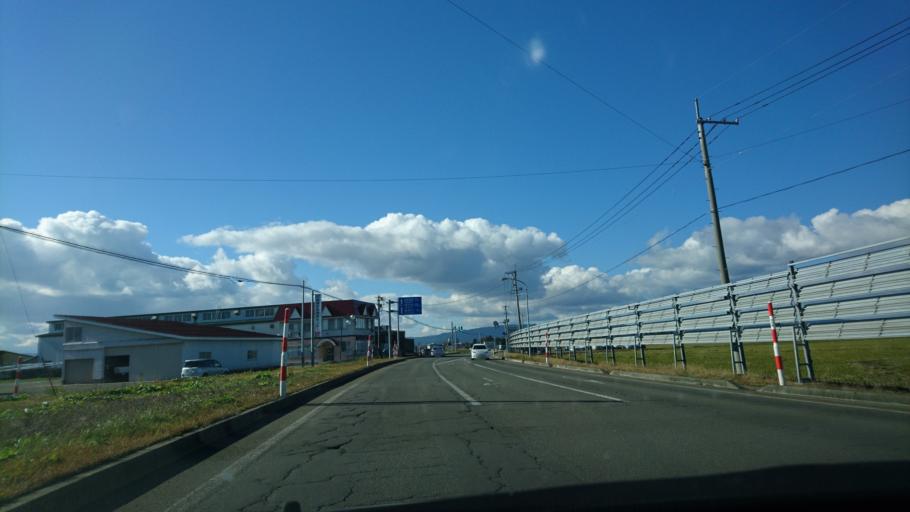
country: JP
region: Akita
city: Yokotemachi
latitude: 39.2659
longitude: 140.4741
